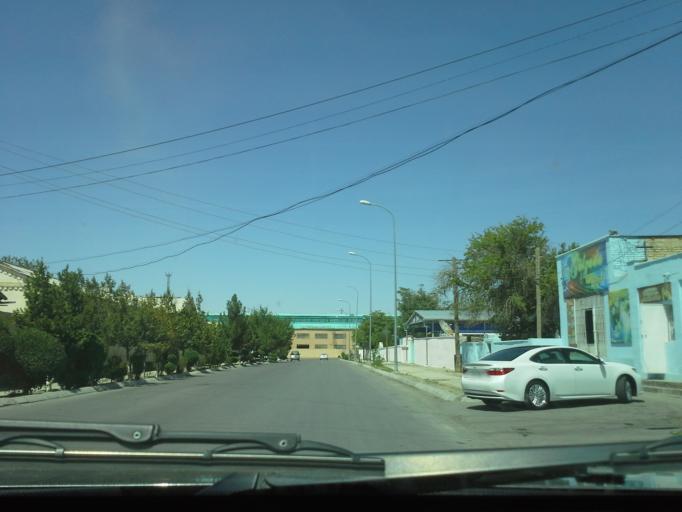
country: TM
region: Balkan
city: Serdar
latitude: 38.9754
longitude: 56.2735
